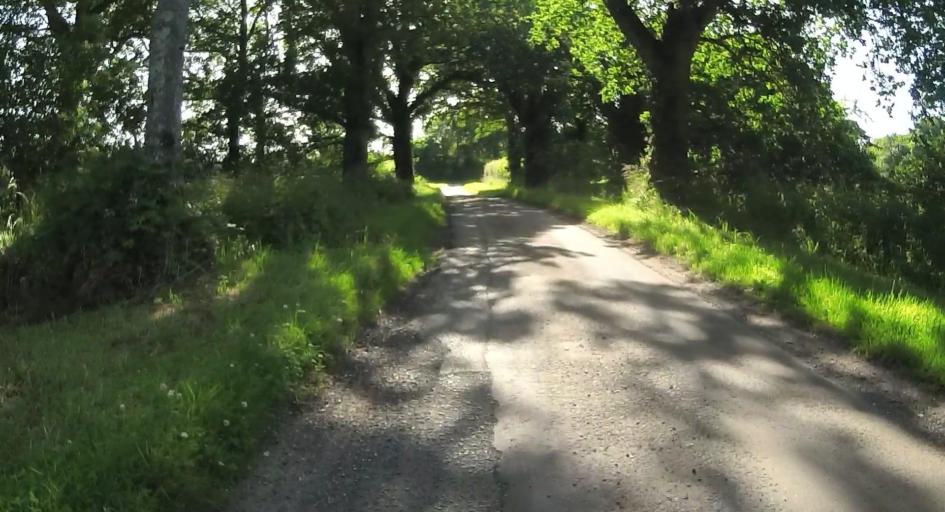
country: GB
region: England
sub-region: Hampshire
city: Long Sutton
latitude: 51.1866
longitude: -0.9418
